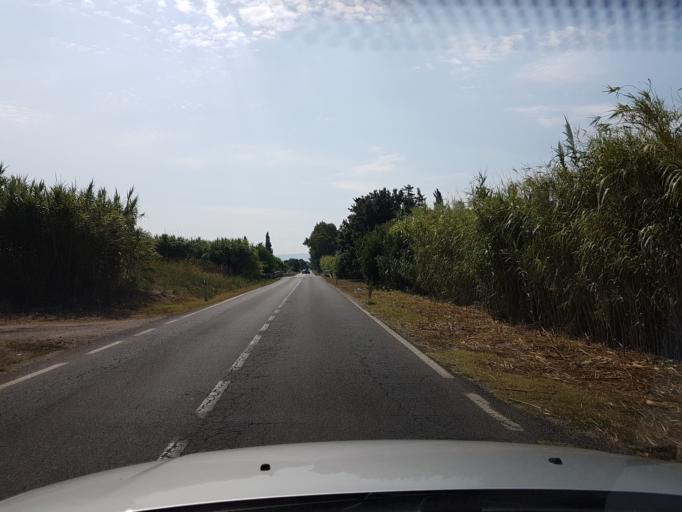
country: IT
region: Sardinia
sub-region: Provincia di Oristano
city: Donigala Fenugheddu
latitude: 39.9476
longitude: 8.5642
